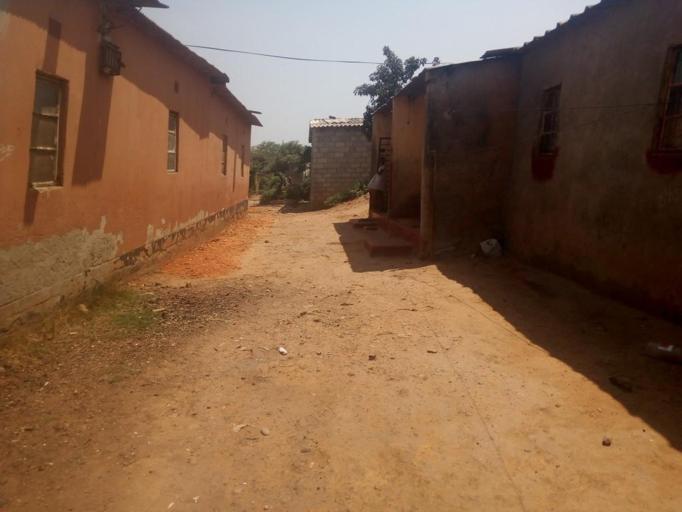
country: ZM
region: Lusaka
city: Lusaka
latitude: -15.4050
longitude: 28.3678
